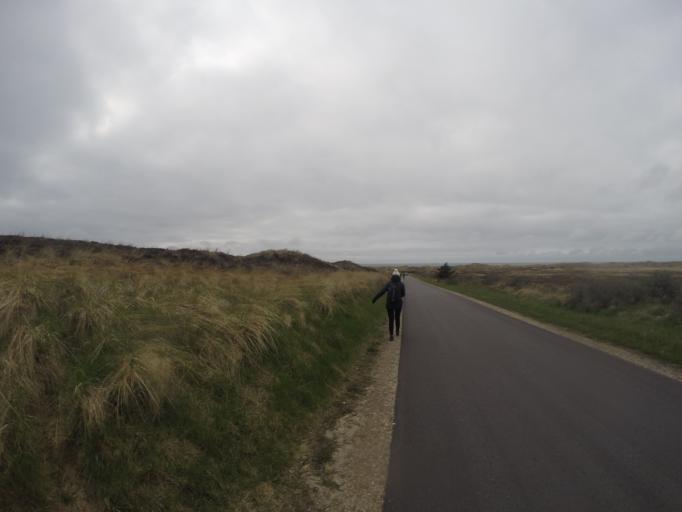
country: DK
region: North Denmark
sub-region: Thisted Kommune
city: Hurup
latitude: 56.9253
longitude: 8.3465
